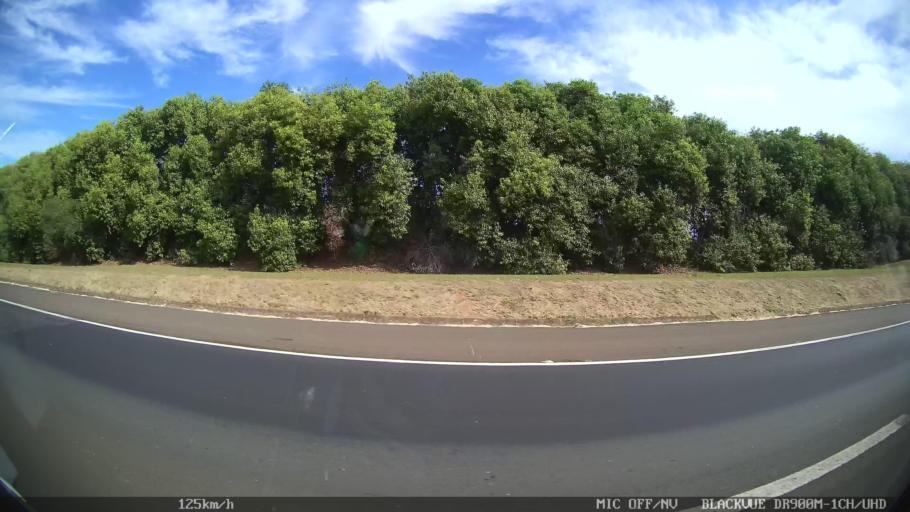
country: BR
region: Sao Paulo
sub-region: Matao
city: Matao
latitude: -21.6122
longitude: -48.4220
